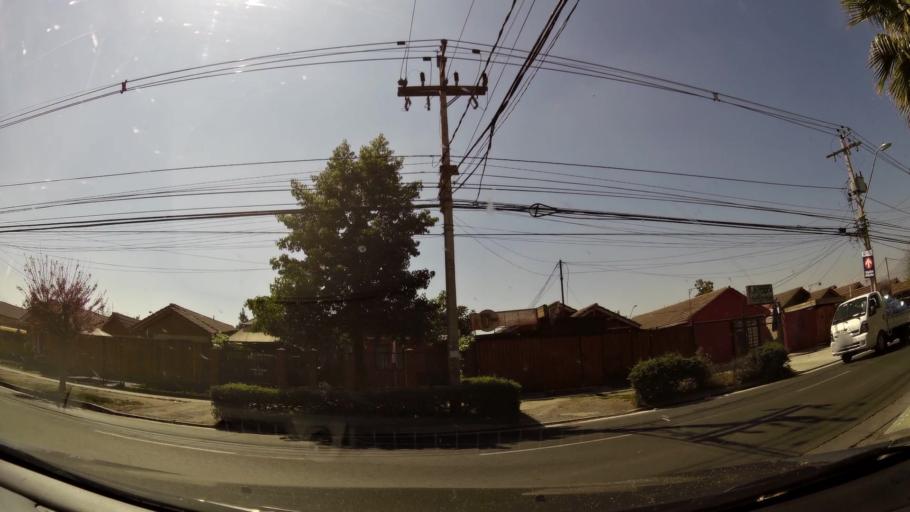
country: CL
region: Santiago Metropolitan
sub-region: Provincia de Santiago
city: Lo Prado
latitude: -33.3539
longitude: -70.7234
